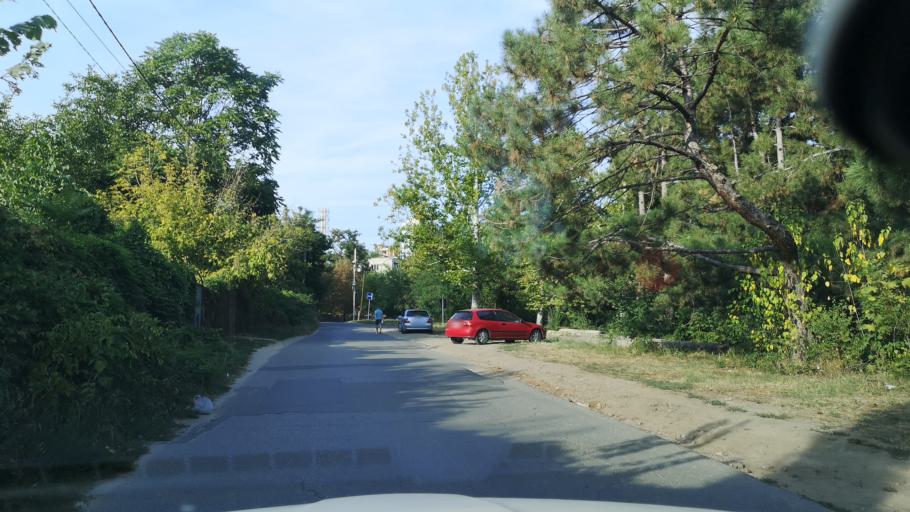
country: MD
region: Chisinau
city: Chisinau
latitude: 47.0040
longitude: 28.8456
